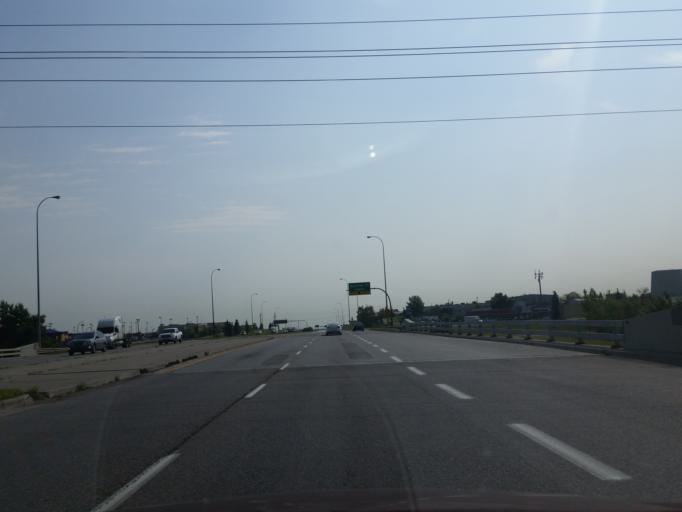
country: CA
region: Alberta
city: Calgary
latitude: 51.0668
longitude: -114.0025
